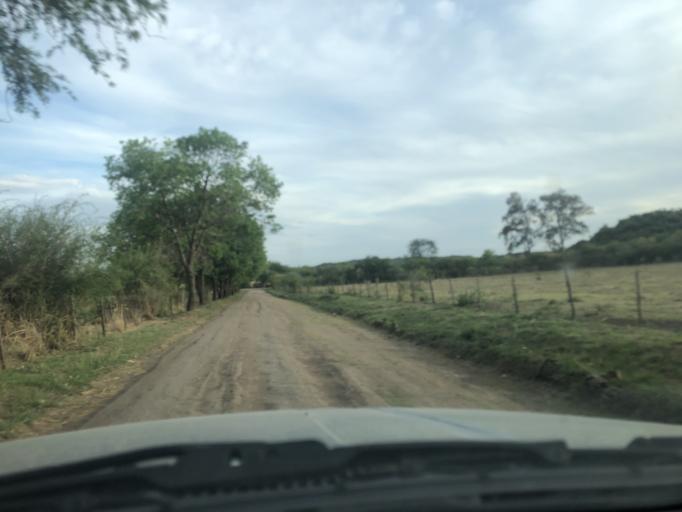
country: AR
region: Cordoba
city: La Granja
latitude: -31.0157
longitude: -64.2517
